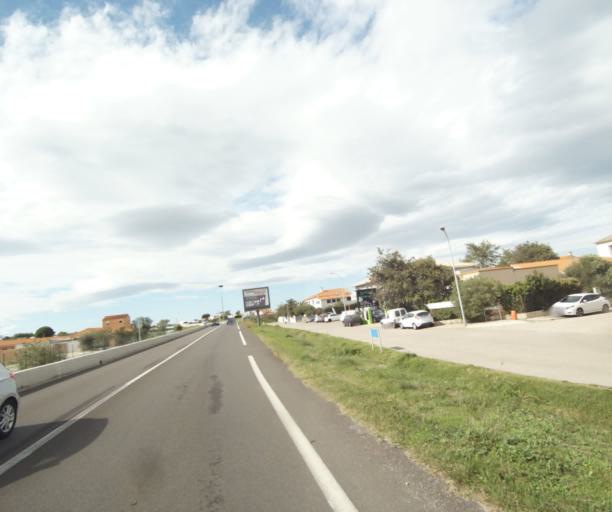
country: FR
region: Languedoc-Roussillon
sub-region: Departement des Pyrenees-Orientales
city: Argelers
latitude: 42.5505
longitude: 3.0117
